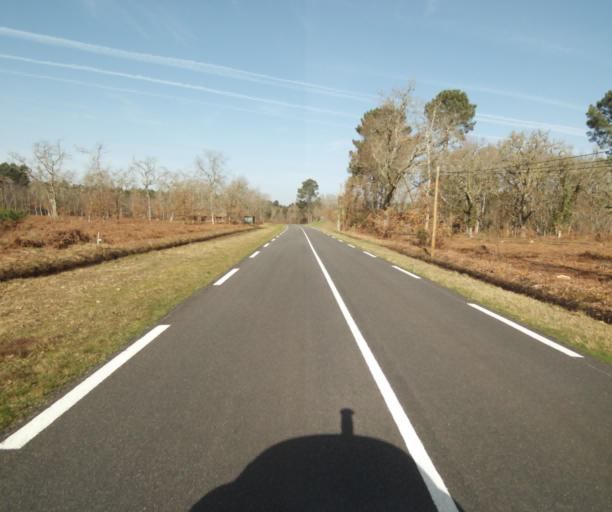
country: FR
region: Aquitaine
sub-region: Departement de la Gironde
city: Grignols
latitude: 44.2143
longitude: -0.1658
